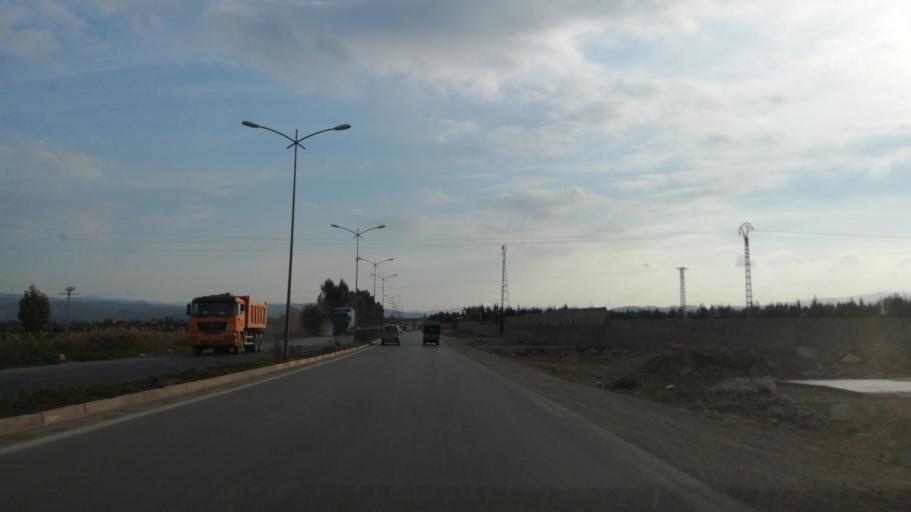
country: DZ
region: Mascara
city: Mascara
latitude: 35.6278
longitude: 0.0614
